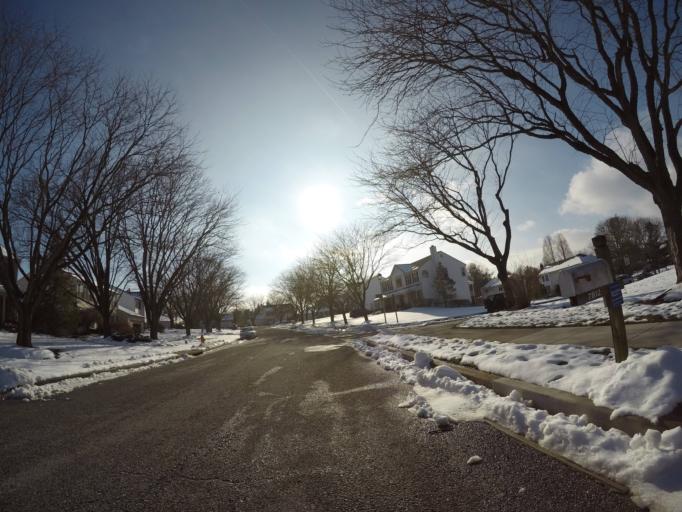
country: US
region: Maryland
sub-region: Howard County
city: Ilchester
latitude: 39.2158
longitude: -76.7832
